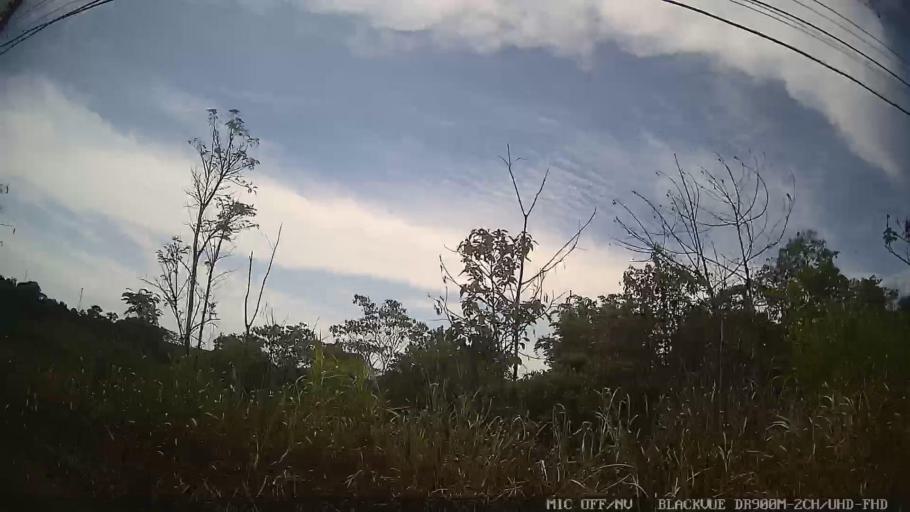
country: BR
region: Sao Paulo
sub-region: Santa Isabel
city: Santa Isabel
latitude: -23.3937
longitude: -46.1844
